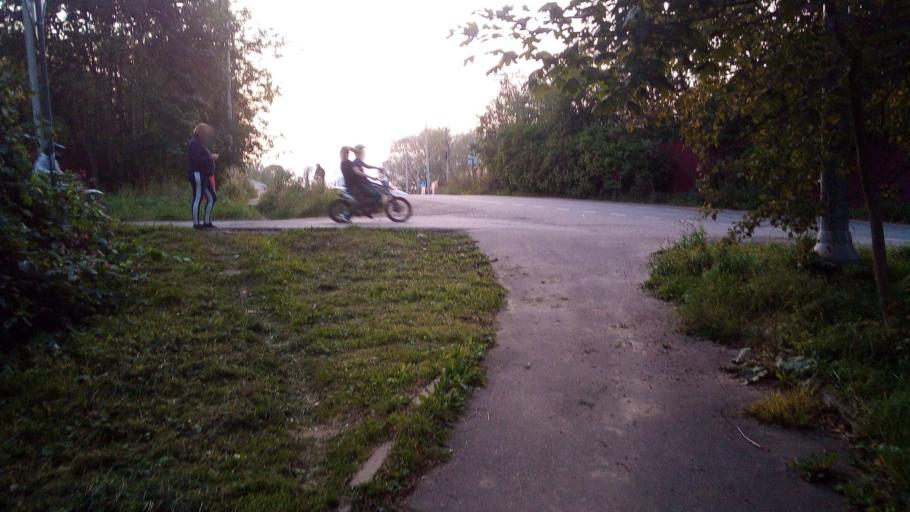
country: RU
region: Moskovskaya
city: Khot'kovo
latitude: 56.2473
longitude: 37.9422
